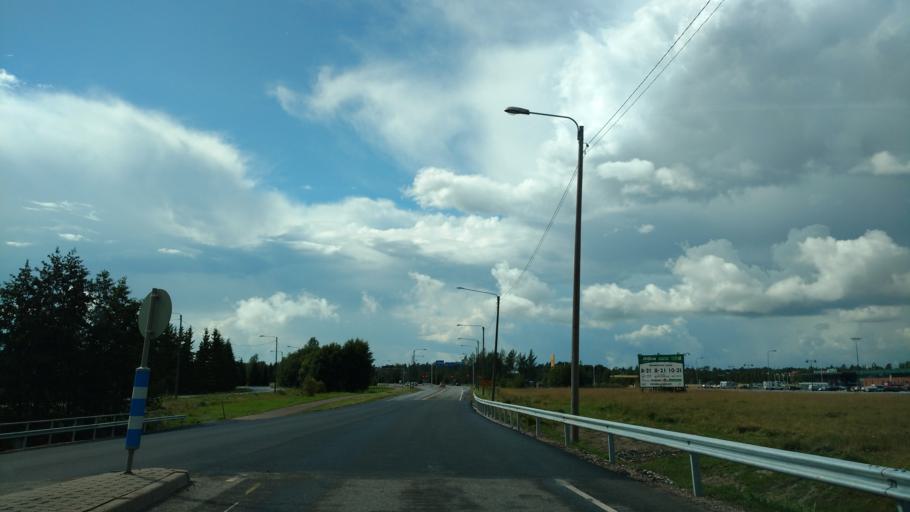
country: FI
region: Varsinais-Suomi
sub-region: Salo
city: Halikko
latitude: 60.3917
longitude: 23.0887
